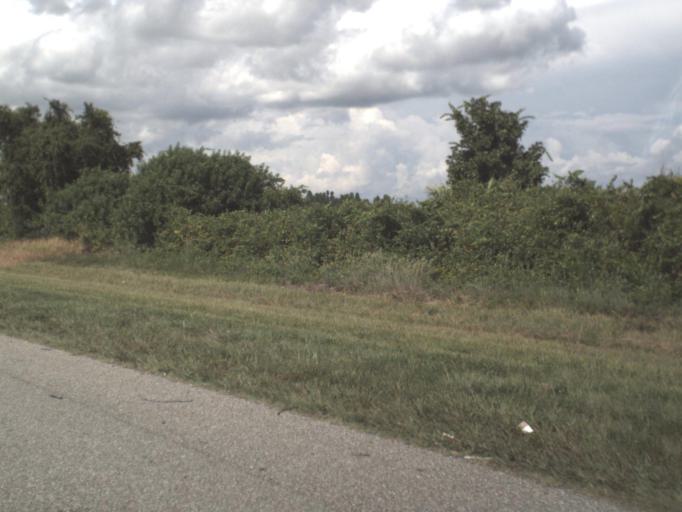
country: US
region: Florida
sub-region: Hillsborough County
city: Apollo Beach
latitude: 27.7577
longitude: -82.3728
